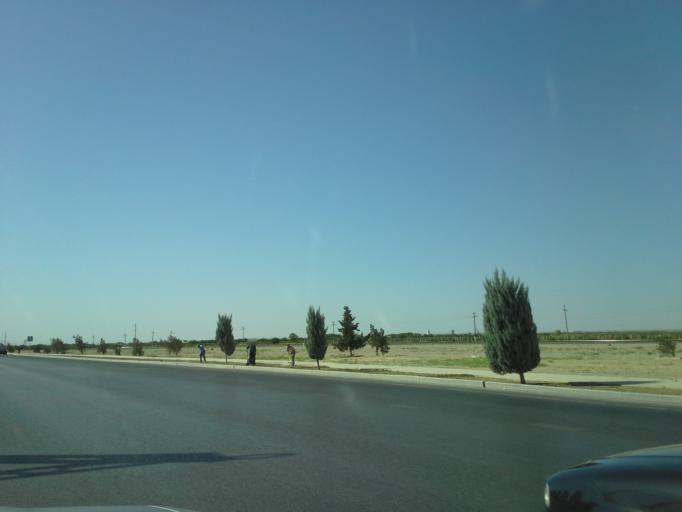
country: TM
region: Ahal
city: Annau
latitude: 37.9143
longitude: 58.4807
